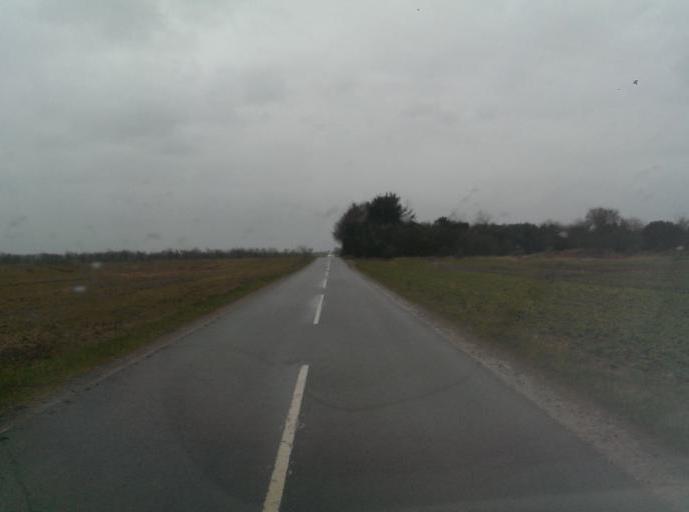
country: DK
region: Central Jutland
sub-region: Ringkobing-Skjern Kommune
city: Skjern
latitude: 56.0548
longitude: 8.4615
